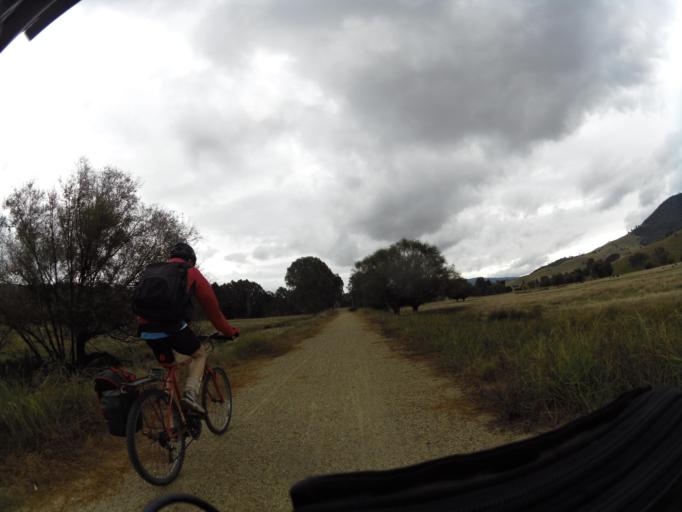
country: AU
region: New South Wales
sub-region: Albury Municipality
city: East Albury
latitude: -36.1938
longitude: 147.3189
